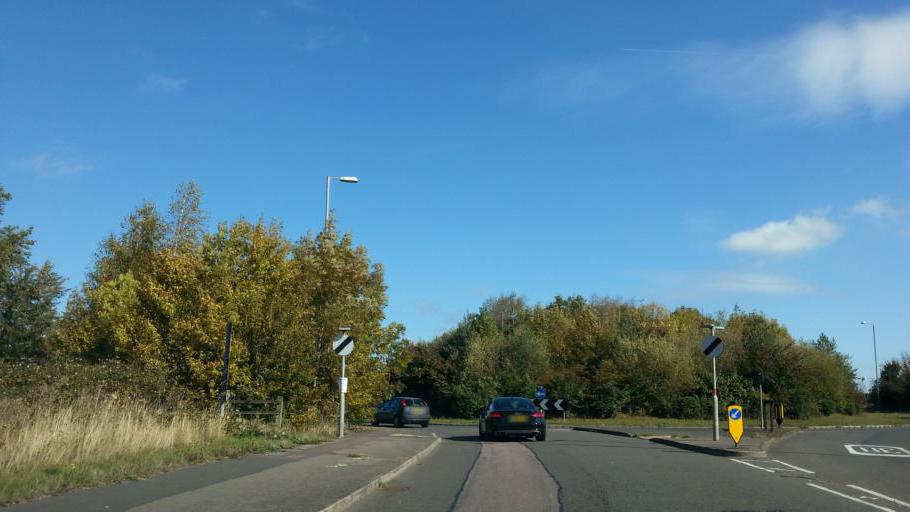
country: GB
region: England
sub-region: Northamptonshire
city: Higham Ferrers
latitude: 52.2999
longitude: -0.5842
